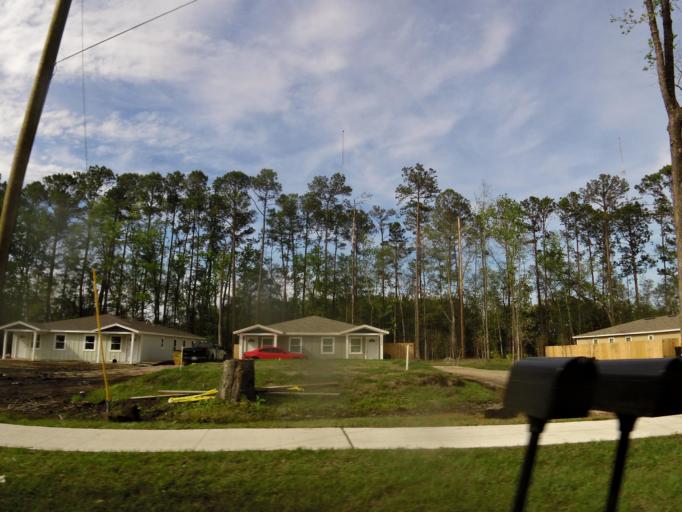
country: US
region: Florida
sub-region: Duval County
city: Jacksonville
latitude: 30.2985
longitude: -81.7617
